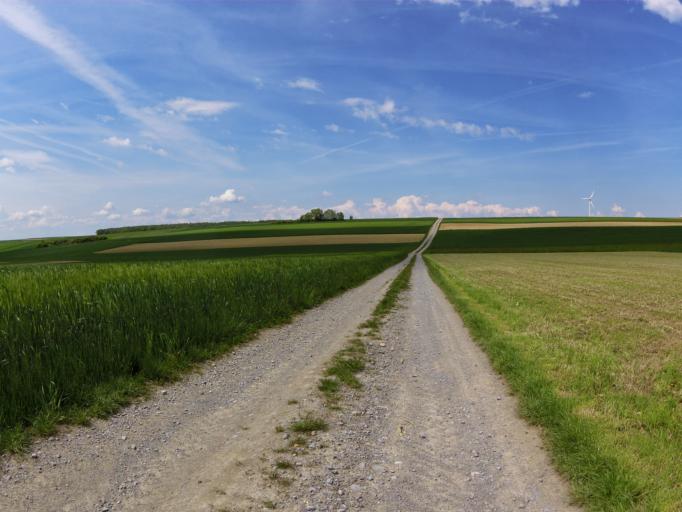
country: DE
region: Bavaria
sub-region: Regierungsbezirk Unterfranken
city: Theilheim
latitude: 49.7336
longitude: 10.0450
